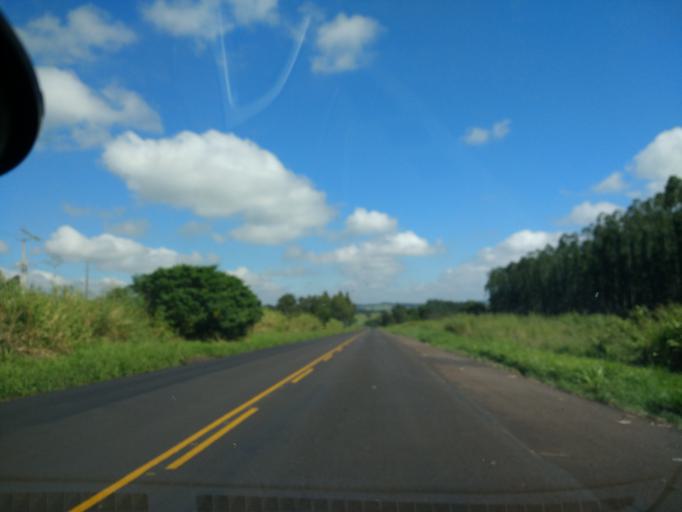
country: BR
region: Parana
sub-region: Cianorte
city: Cianorte
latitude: -23.7344
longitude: -52.7043
